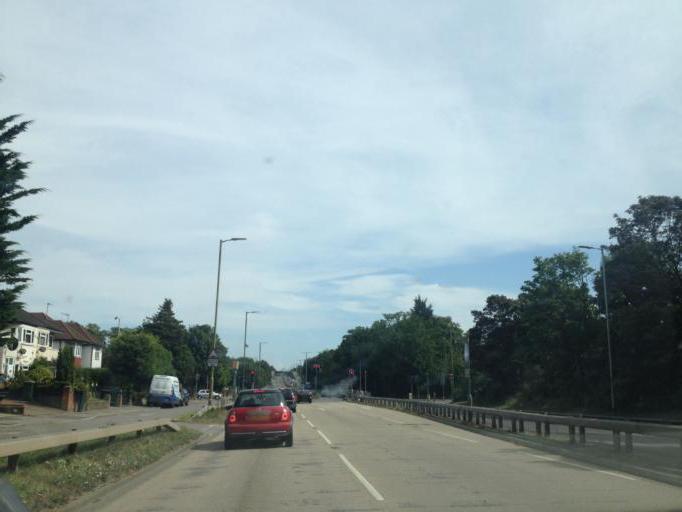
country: GB
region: England
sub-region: Hertfordshire
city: Watford
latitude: 51.6769
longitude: -0.3798
